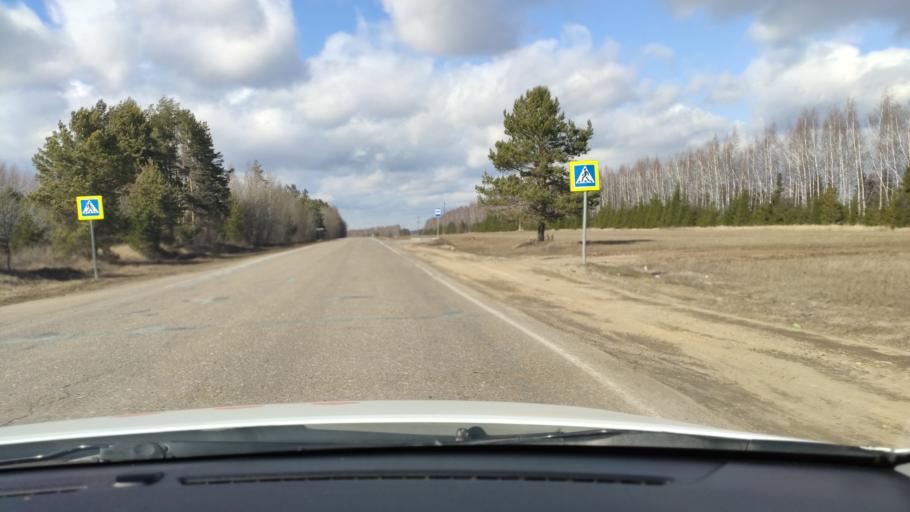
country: RU
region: Tatarstan
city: Vysokaya Gora
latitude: 56.0663
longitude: 49.2006
